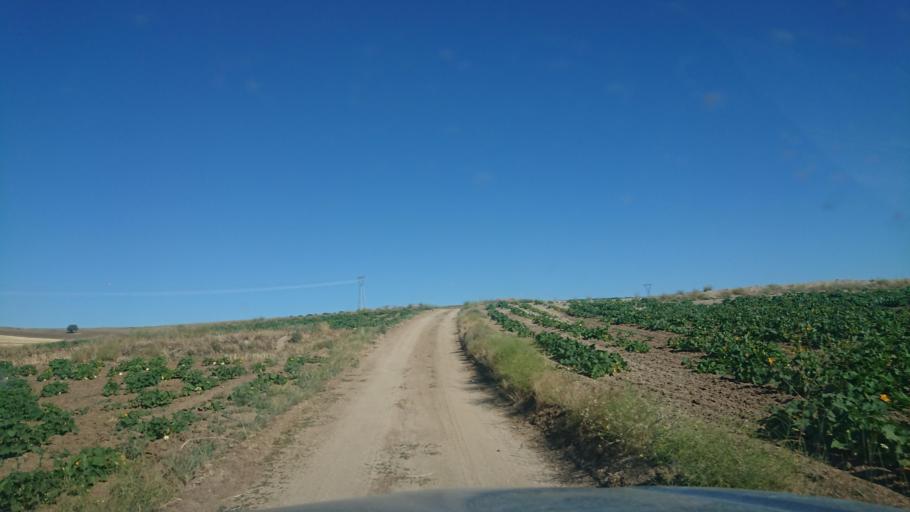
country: TR
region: Aksaray
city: Agacoren
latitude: 38.8321
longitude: 33.9501
